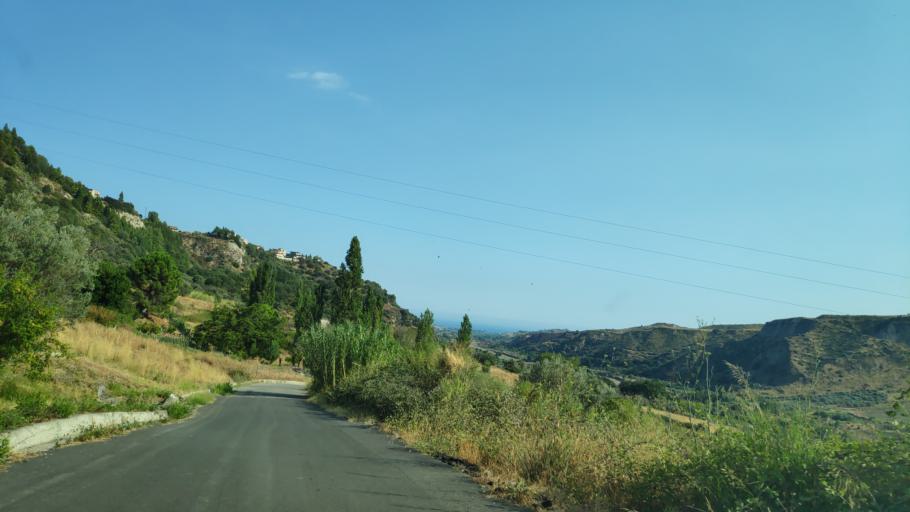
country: IT
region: Calabria
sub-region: Provincia di Reggio Calabria
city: Placanica
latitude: 38.4143
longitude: 16.4453
